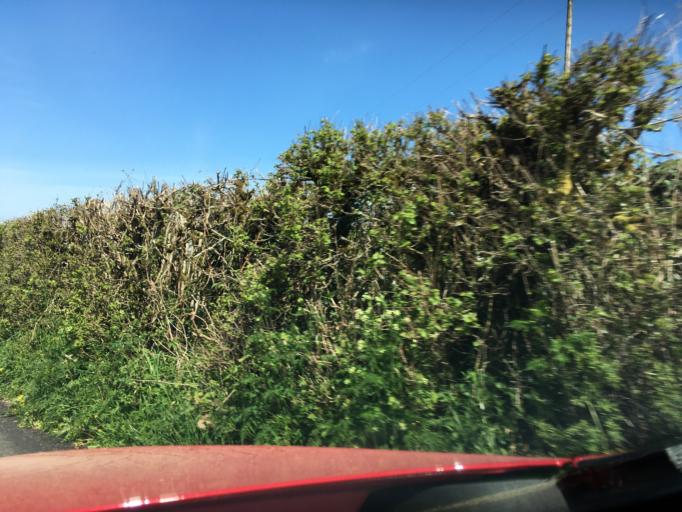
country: GB
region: Wales
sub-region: Monmouthshire
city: Llangwm
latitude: 51.7657
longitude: -2.8294
